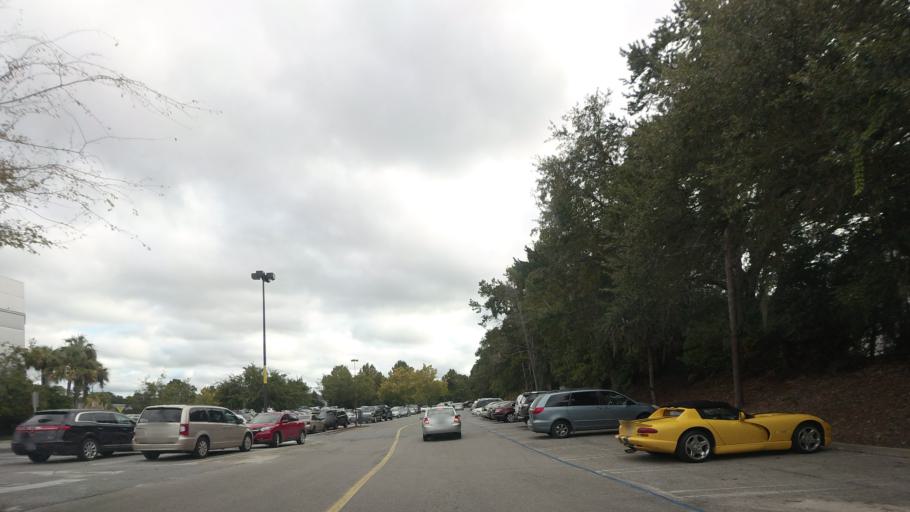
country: US
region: Florida
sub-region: Alachua County
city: Gainesville
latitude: 29.6546
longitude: -82.4118
